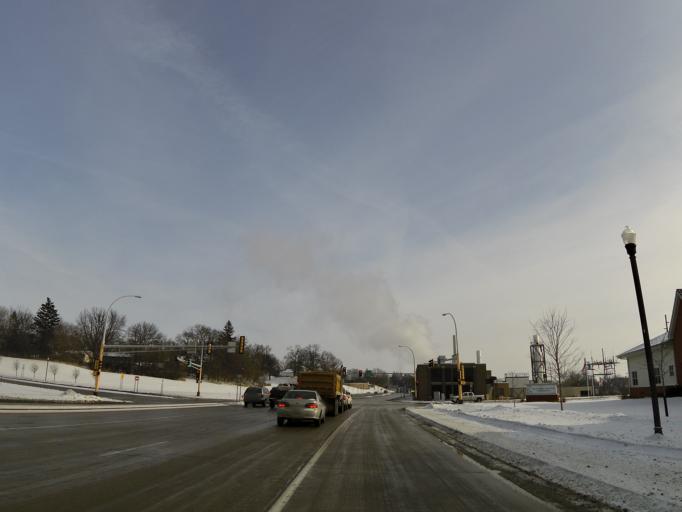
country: US
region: Minnesota
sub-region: McLeod County
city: Hutchinson
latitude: 44.8968
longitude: -94.3704
